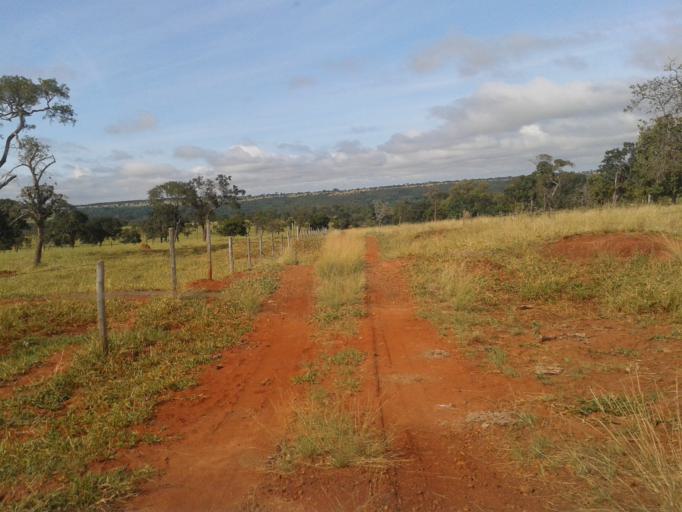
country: BR
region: Minas Gerais
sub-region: Campina Verde
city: Campina Verde
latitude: -19.4164
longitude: -49.6564
